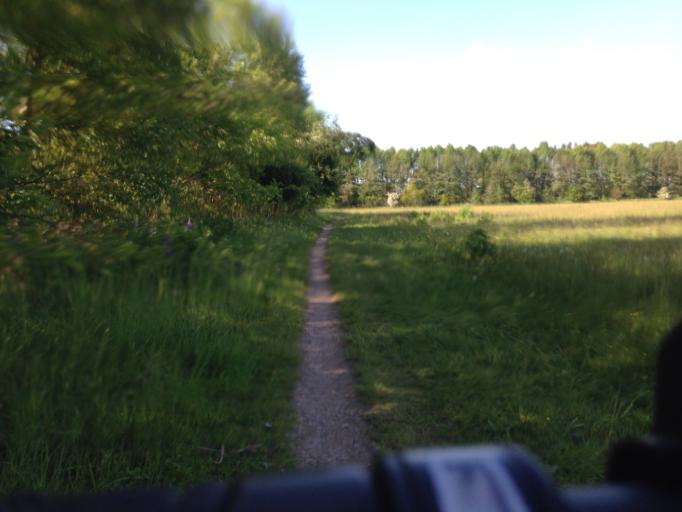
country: DE
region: Schleswig-Holstein
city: Braak
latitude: 53.6317
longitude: 10.2276
